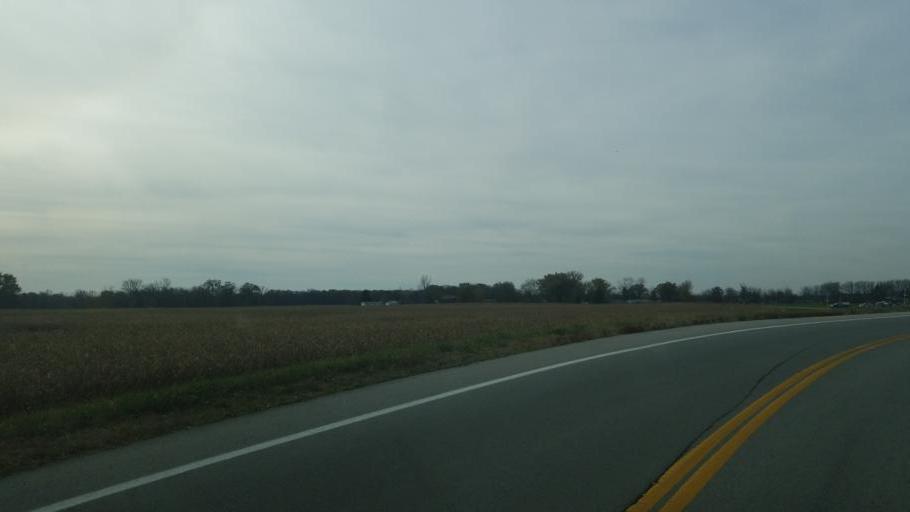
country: US
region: Ohio
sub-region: Madison County
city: London
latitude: 39.9368
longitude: -83.3983
